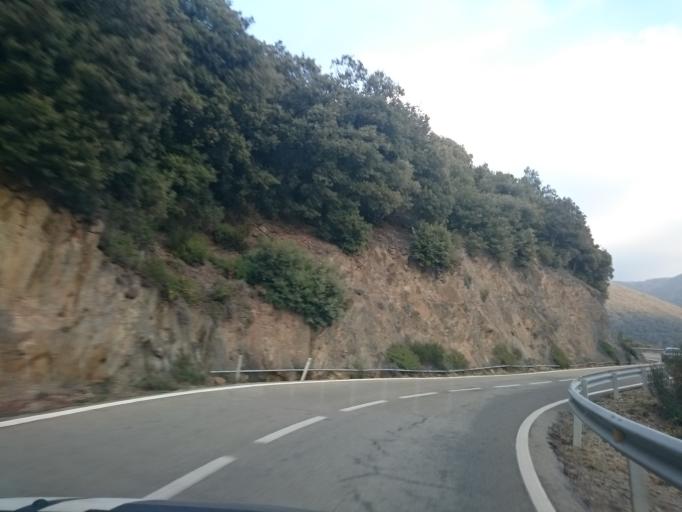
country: ES
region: Catalonia
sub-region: Provincia de Barcelona
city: Seva
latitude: 41.8167
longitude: 2.3184
